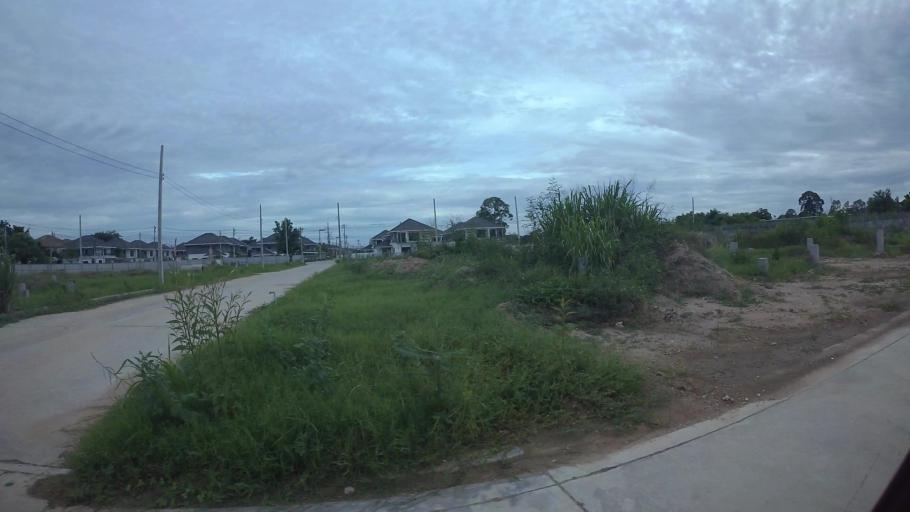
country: TH
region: Chon Buri
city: Si Racha
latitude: 13.1364
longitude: 100.9638
